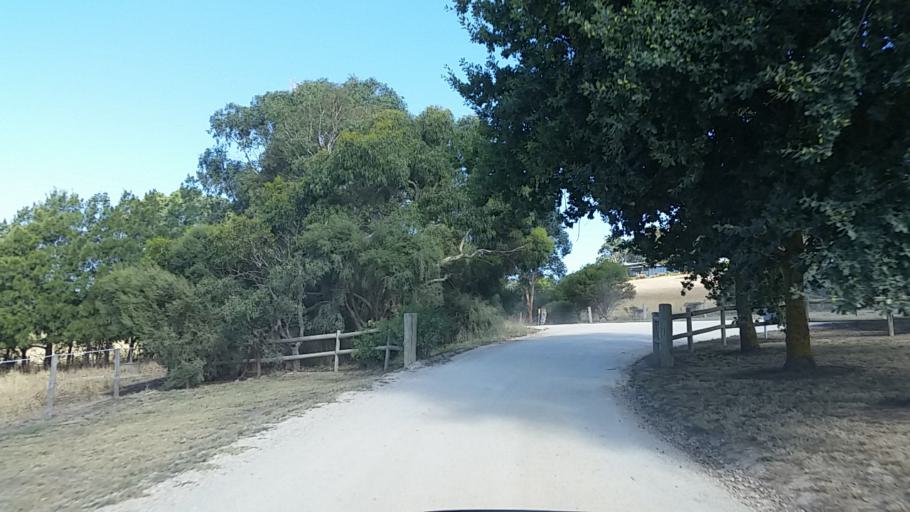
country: AU
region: South Australia
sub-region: Adelaide Hills
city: Balhannah
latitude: -35.0153
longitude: 138.8397
